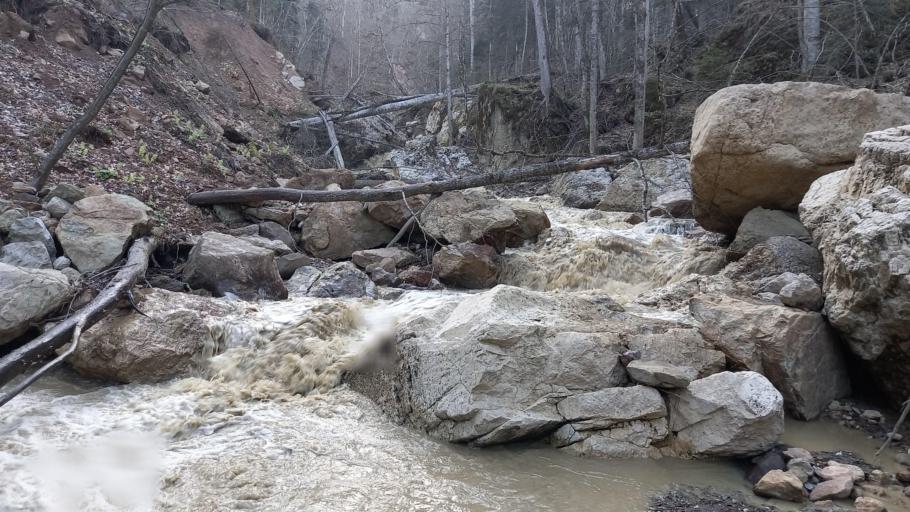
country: RU
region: Adygeya
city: Kamennomostskiy
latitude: 44.0984
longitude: 40.0851
